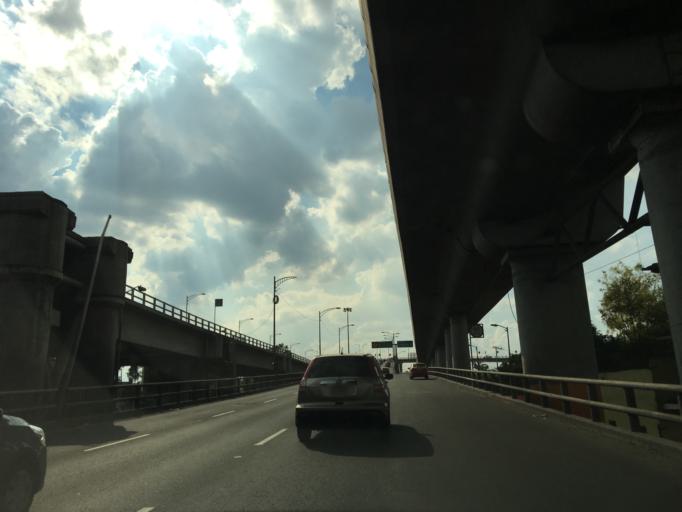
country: MX
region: Mexico City
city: Venustiano Carranza
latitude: 19.4351
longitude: -99.1071
